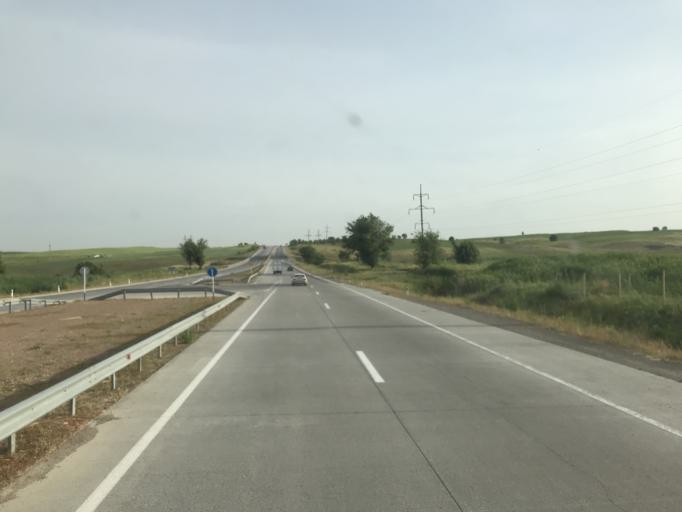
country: KZ
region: Ongtustik Qazaqstan
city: Qazyqurt
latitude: 41.5954
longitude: 69.4060
